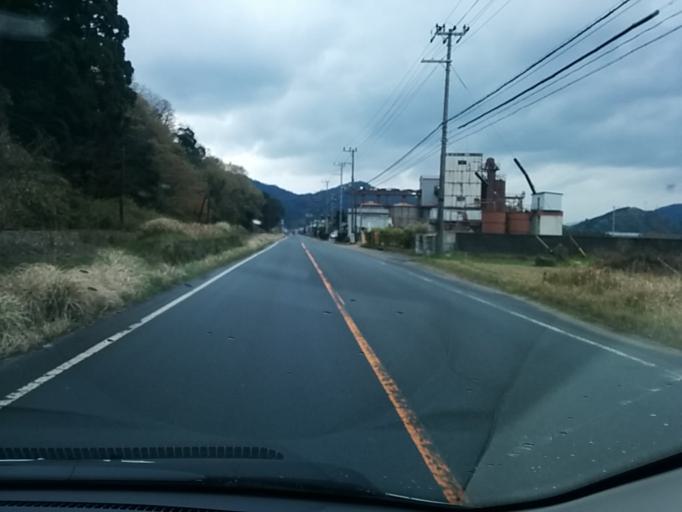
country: JP
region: Kyoto
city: Miyazu
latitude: 35.5607
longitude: 135.1681
